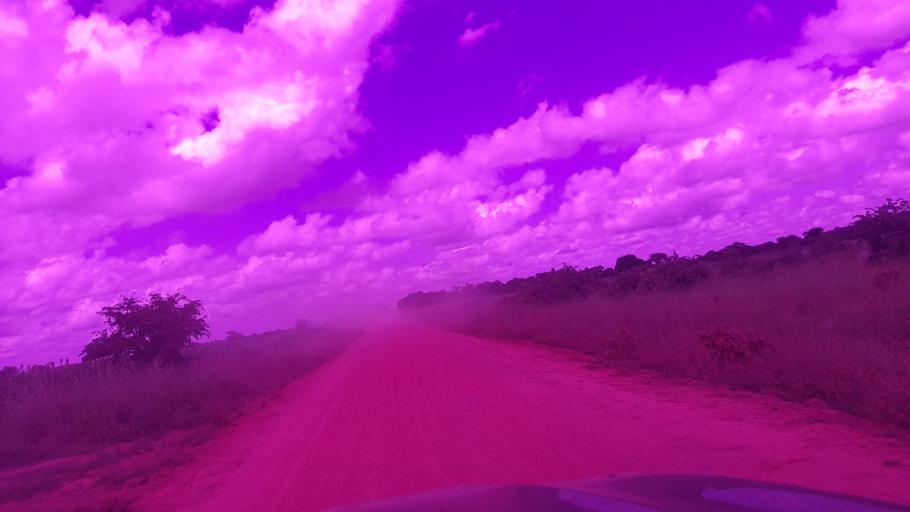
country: ZM
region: Central
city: Chibombo
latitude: -14.7126
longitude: 27.9867
